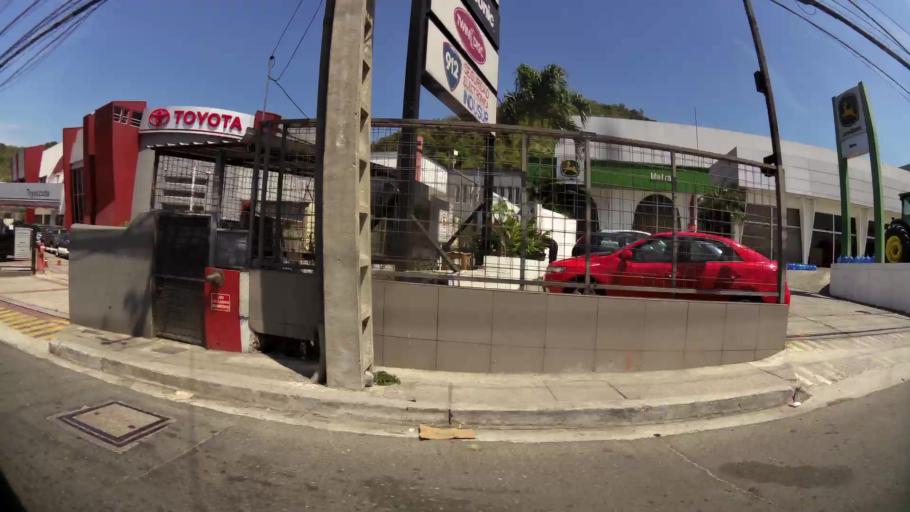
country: EC
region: Guayas
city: Guayaquil
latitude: -2.1655
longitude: -79.9230
